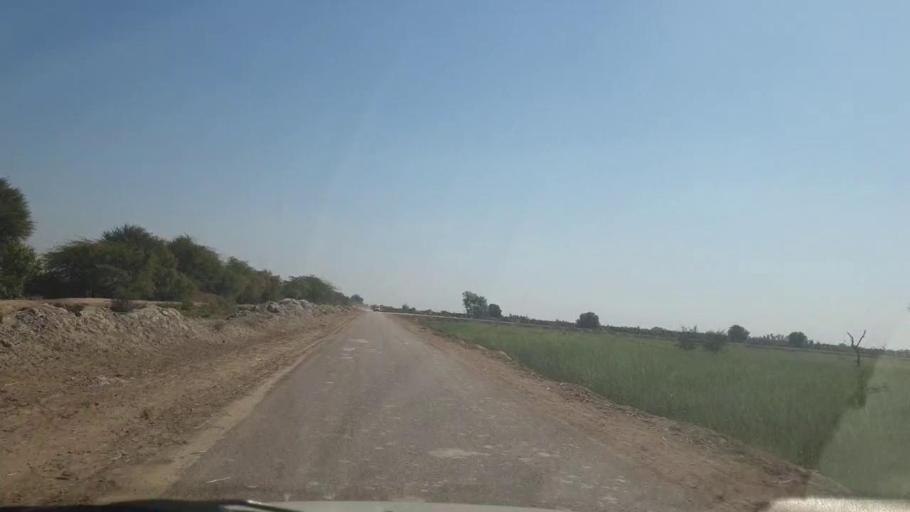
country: PK
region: Sindh
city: Mirpur Khas
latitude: 25.4619
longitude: 69.1805
